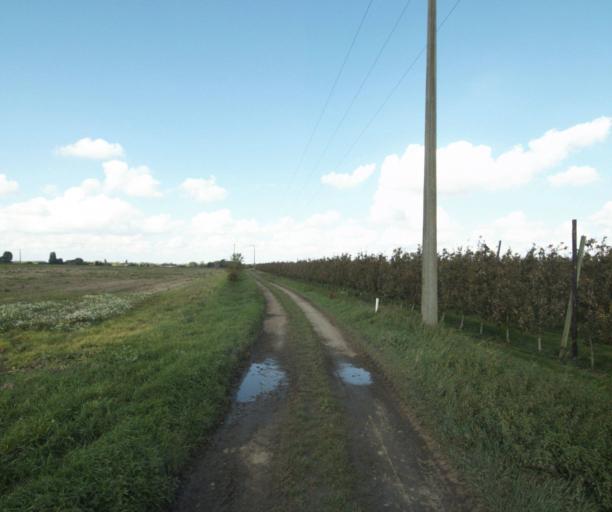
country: FR
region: Nord-Pas-de-Calais
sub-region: Departement du Nord
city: Aubers
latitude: 50.5829
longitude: 2.8261
